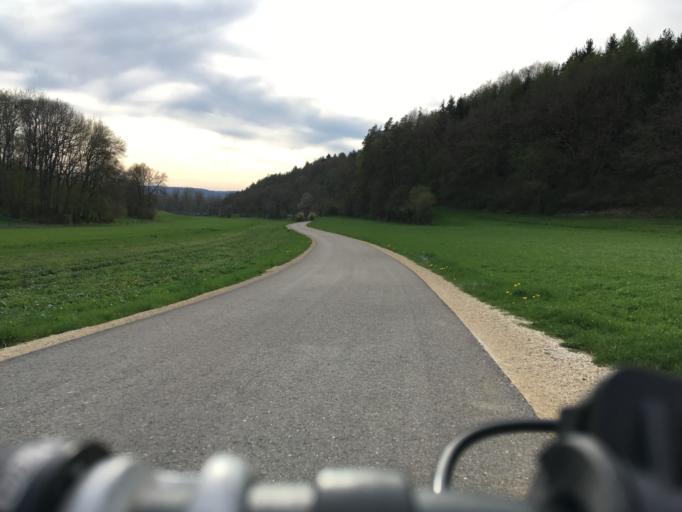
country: DE
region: Baden-Wuerttemberg
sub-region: Freiburg Region
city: Neuhausen
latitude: 47.8091
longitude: 8.7520
